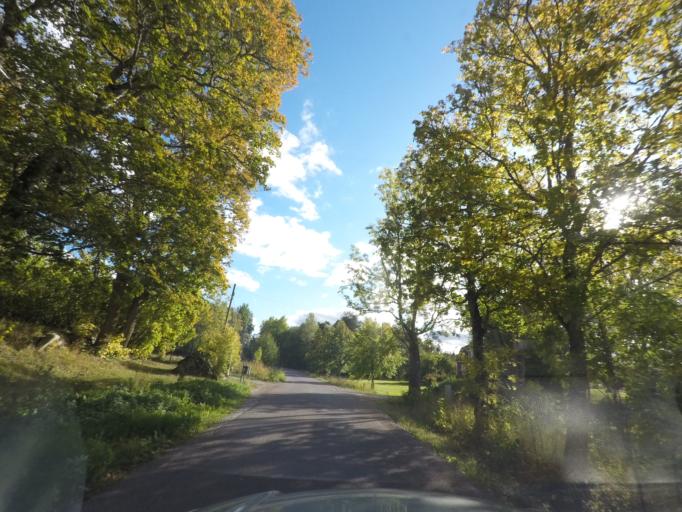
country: SE
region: Vaestmanland
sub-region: Hallstahammars Kommun
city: Kolback
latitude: 59.4974
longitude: 16.1882
